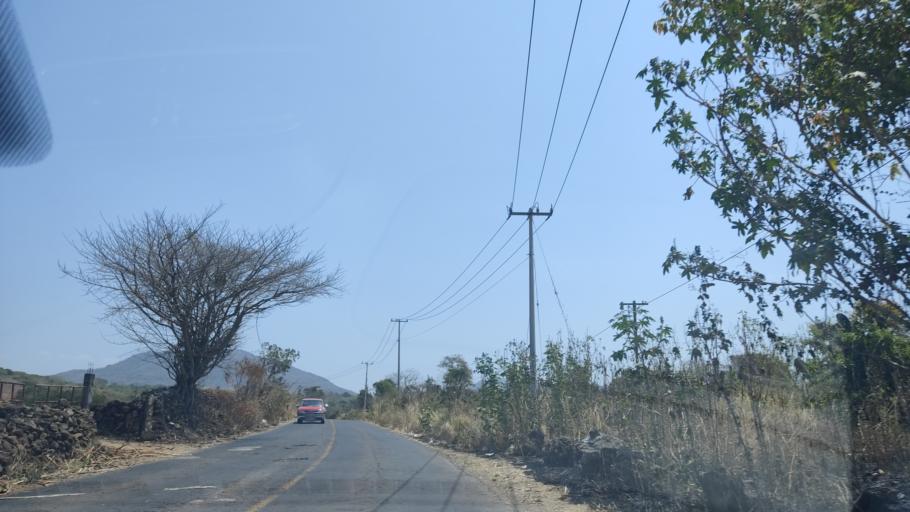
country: MX
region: Nayarit
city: Puga
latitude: 21.5882
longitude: -104.8025
